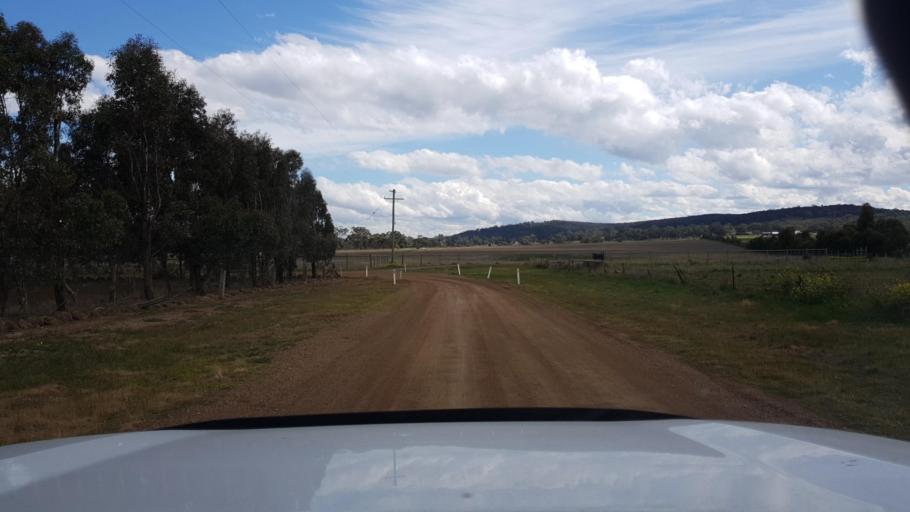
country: AU
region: Victoria
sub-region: Melton
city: Kurunjang
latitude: -37.6077
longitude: 144.6293
